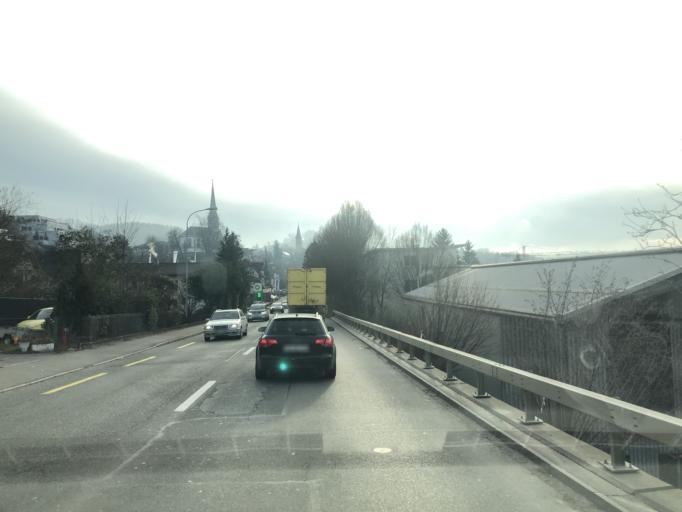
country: CH
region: Aargau
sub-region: Bezirk Baden
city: Gebenstorf
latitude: 47.4853
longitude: 8.2426
